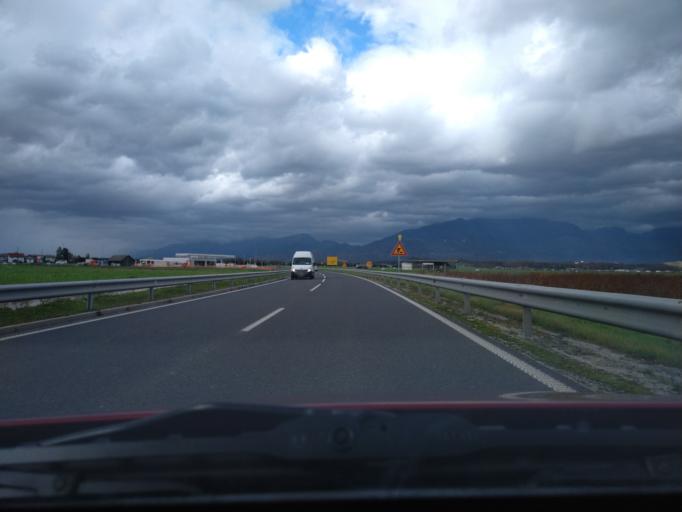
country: SI
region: Menges
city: Menges
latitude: 46.1713
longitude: 14.5794
